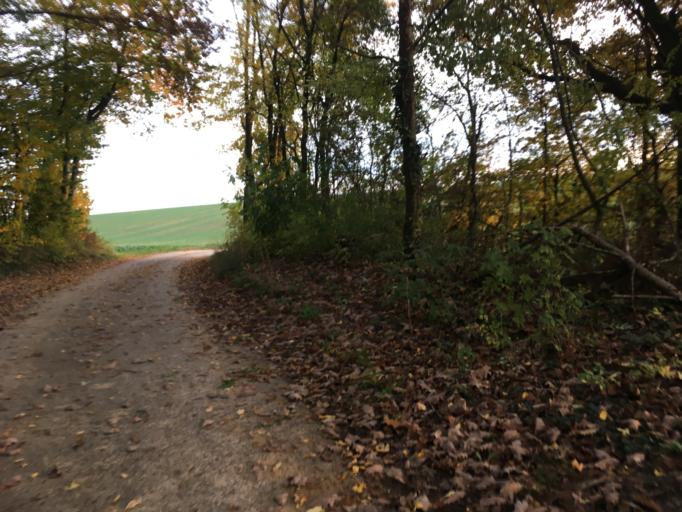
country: DE
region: Baden-Wuerttemberg
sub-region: Regierungsbezirk Stuttgart
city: Kirchardt
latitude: 49.2407
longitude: 8.9860
